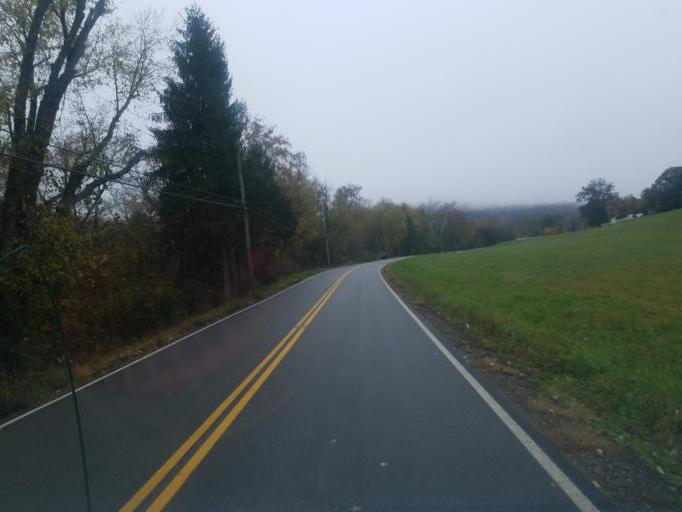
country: US
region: Ohio
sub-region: Morgan County
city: McConnelsville
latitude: 39.6388
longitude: -81.8425
